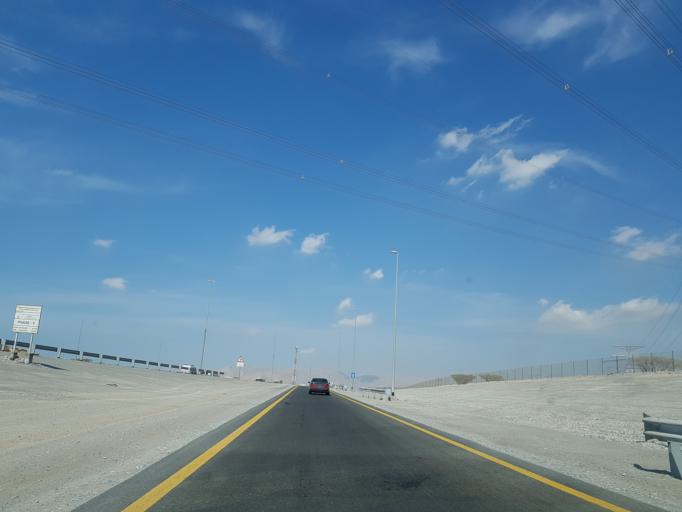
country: AE
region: Ra's al Khaymah
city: Ras al-Khaimah
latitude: 25.7652
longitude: 56.0243
